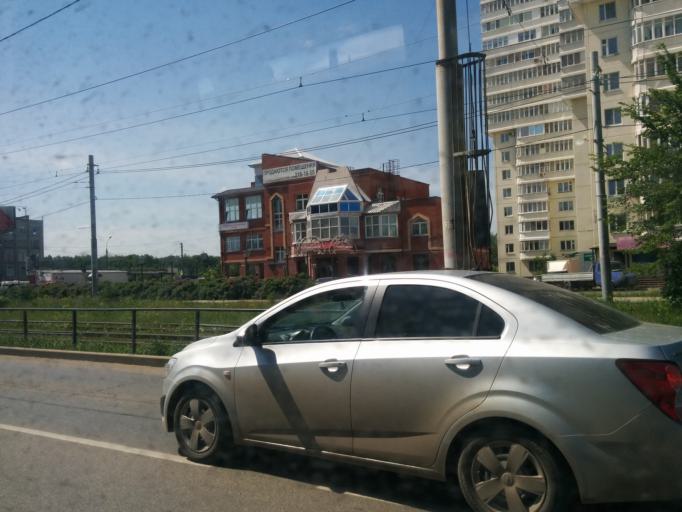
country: RU
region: Perm
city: Perm
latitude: 57.9954
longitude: 56.2876
